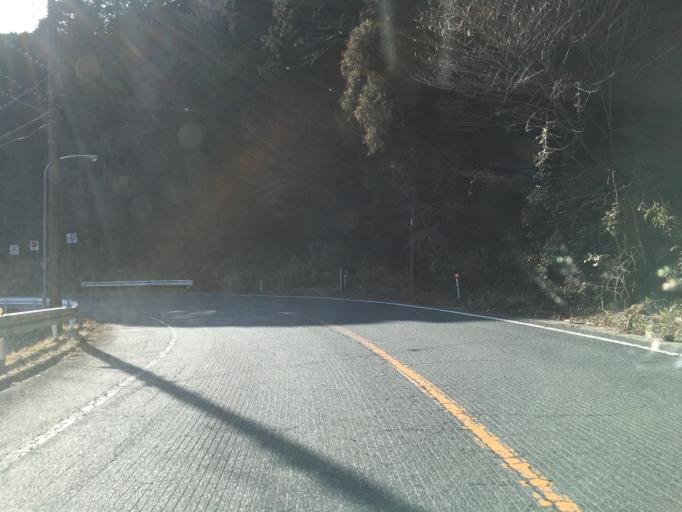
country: JP
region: Ibaraki
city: Takahagi
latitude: 36.7257
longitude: 140.6377
